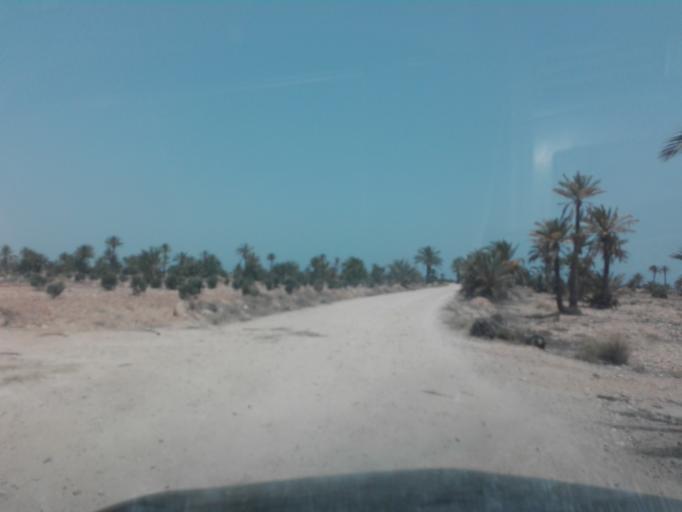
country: TN
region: Safaqis
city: Al Qarmadah
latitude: 34.6652
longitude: 11.0927
